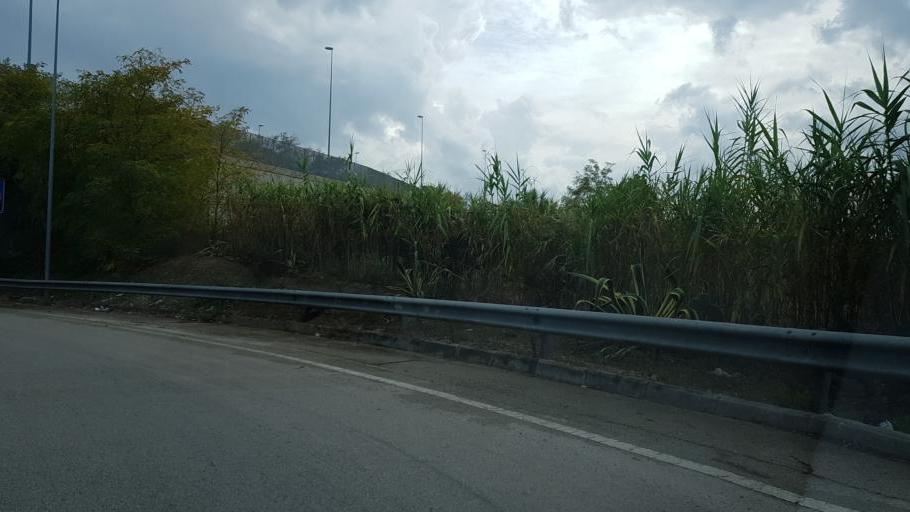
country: IT
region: Apulia
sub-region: Provincia di Bari
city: Triggiano
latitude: 41.0858
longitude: 16.8940
